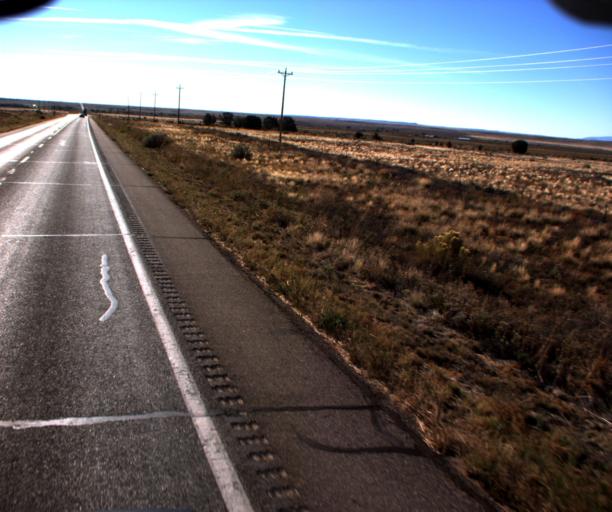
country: US
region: Arizona
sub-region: Mohave County
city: Colorado City
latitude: 36.9504
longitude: -112.9589
